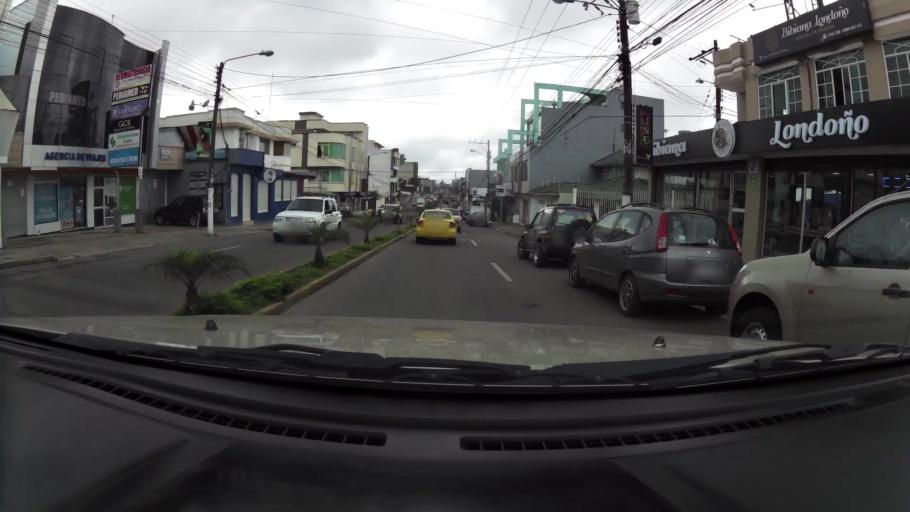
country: EC
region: Santo Domingo de los Tsachilas
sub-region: Canton Santo Domingo de los Colorados
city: Santo Domingo de los Colorados
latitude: -0.2493
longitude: -79.1523
